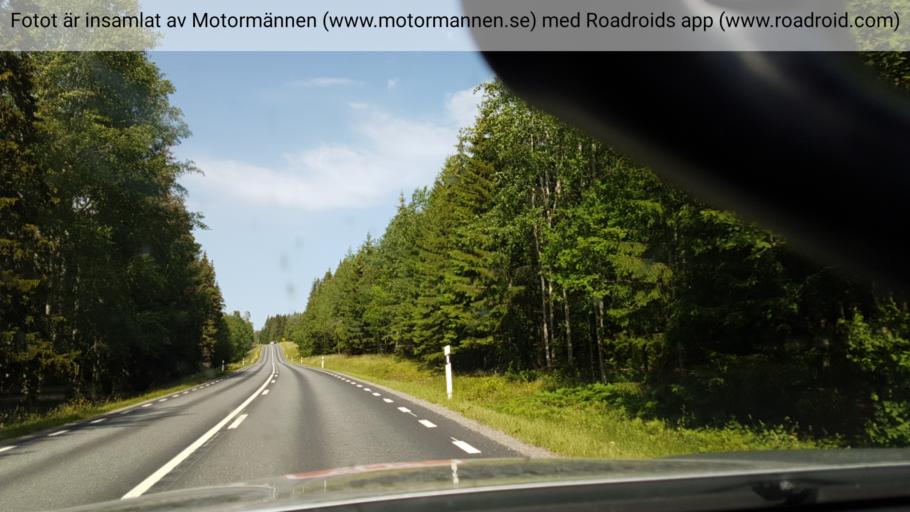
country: SE
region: Joenkoeping
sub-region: Aneby Kommun
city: Aneby
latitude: 57.8928
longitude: 14.8855
